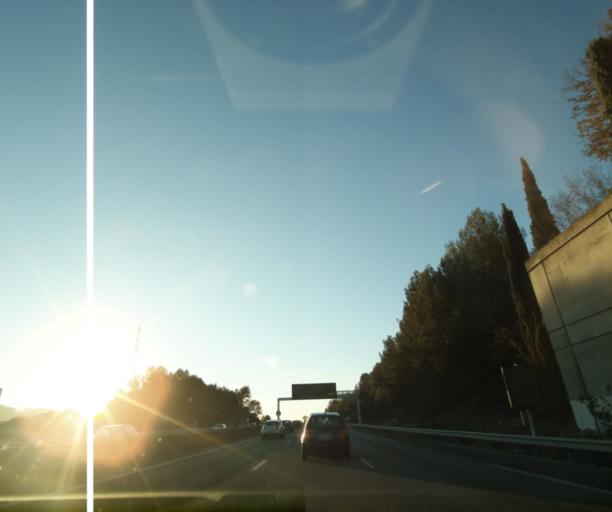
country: FR
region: Provence-Alpes-Cote d'Azur
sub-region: Departement des Bouches-du-Rhone
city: Meyreuil
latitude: 43.5132
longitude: 5.4781
